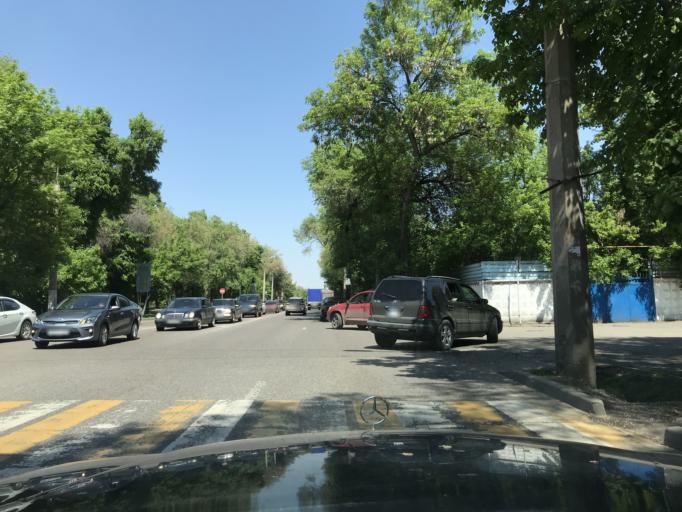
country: KZ
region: Almaty Oblysy
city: Pervomayskiy
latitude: 43.3286
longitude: 76.9598
